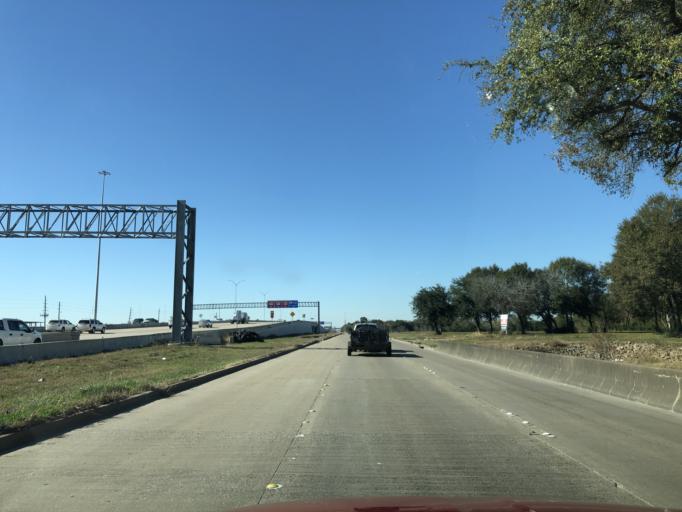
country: US
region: Texas
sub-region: Brazoria County
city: Brookside Village
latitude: 29.5975
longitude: -95.3961
